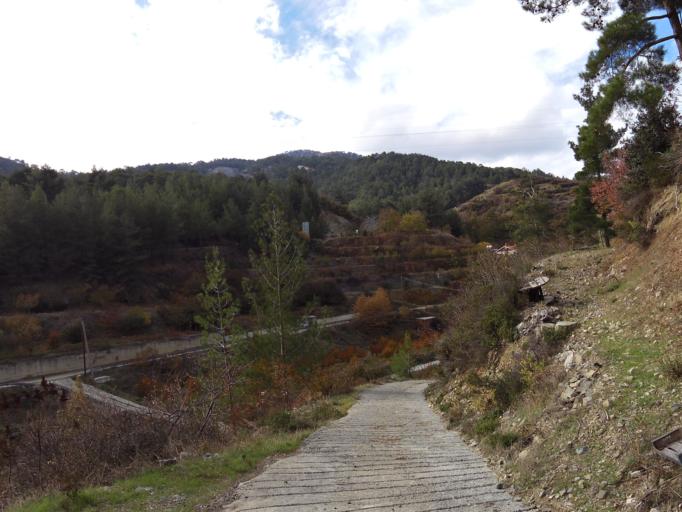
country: CY
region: Limassol
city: Kyperounta
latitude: 34.9327
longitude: 32.9358
